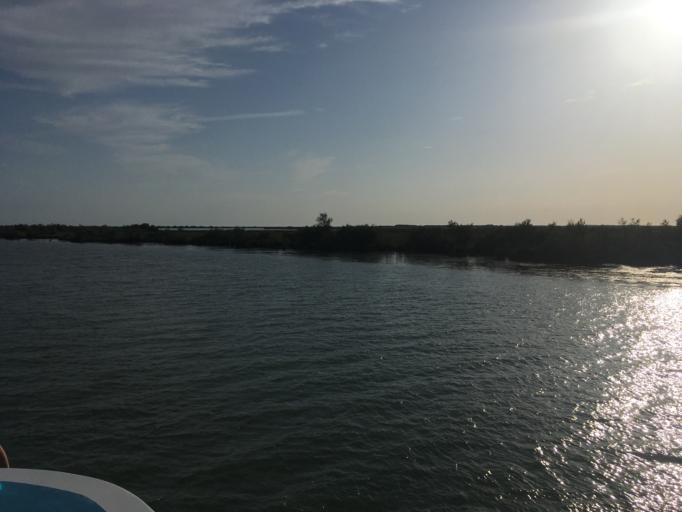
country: FR
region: Provence-Alpes-Cote d'Azur
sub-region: Departement des Bouches-du-Rhone
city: Saintes-Maries-de-la-Mer
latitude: 43.4620
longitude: 4.3904
